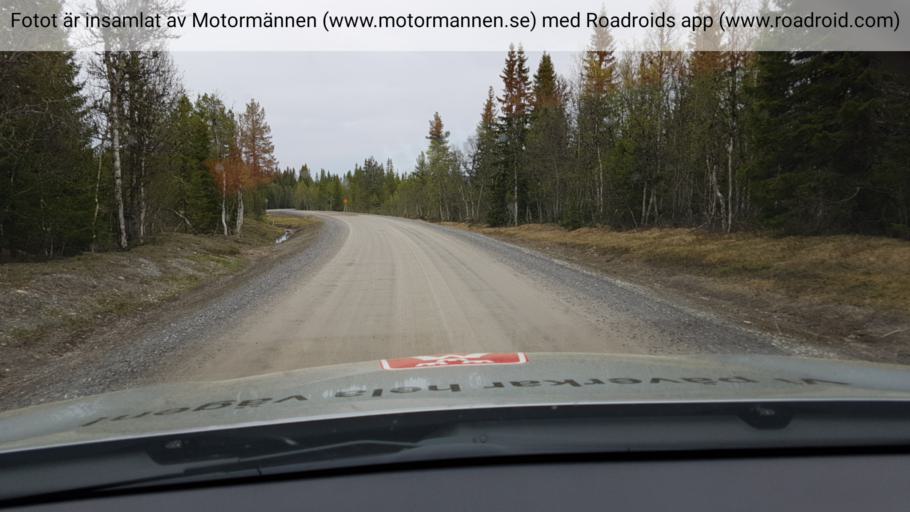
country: NO
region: Nord-Trondelag
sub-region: Snasa
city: Snaase
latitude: 63.7298
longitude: 12.4705
